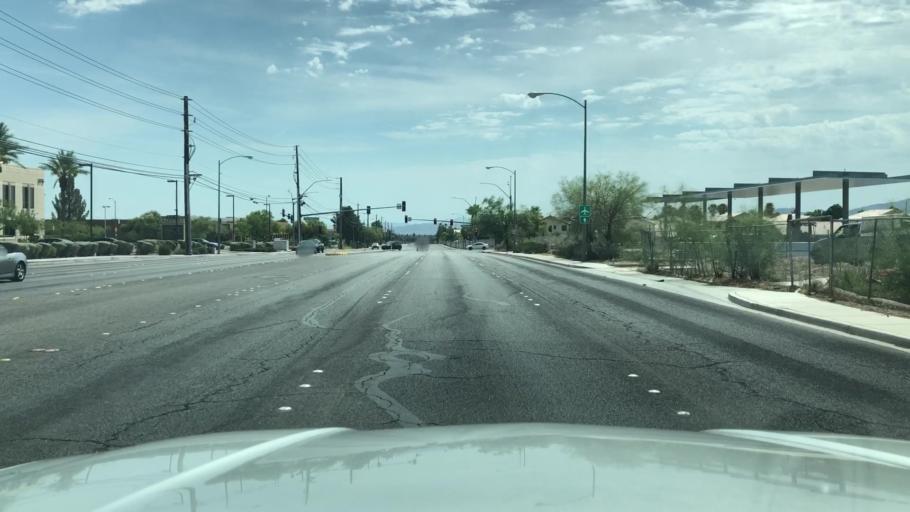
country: US
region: Nevada
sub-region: Clark County
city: Paradise
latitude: 36.0569
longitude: -115.1561
